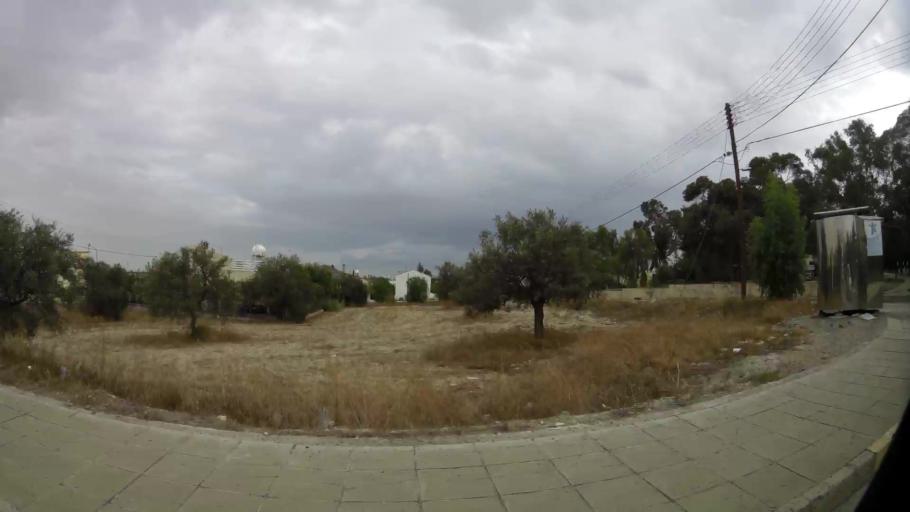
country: CY
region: Lefkosia
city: Geri
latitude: 35.1146
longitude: 33.3843
